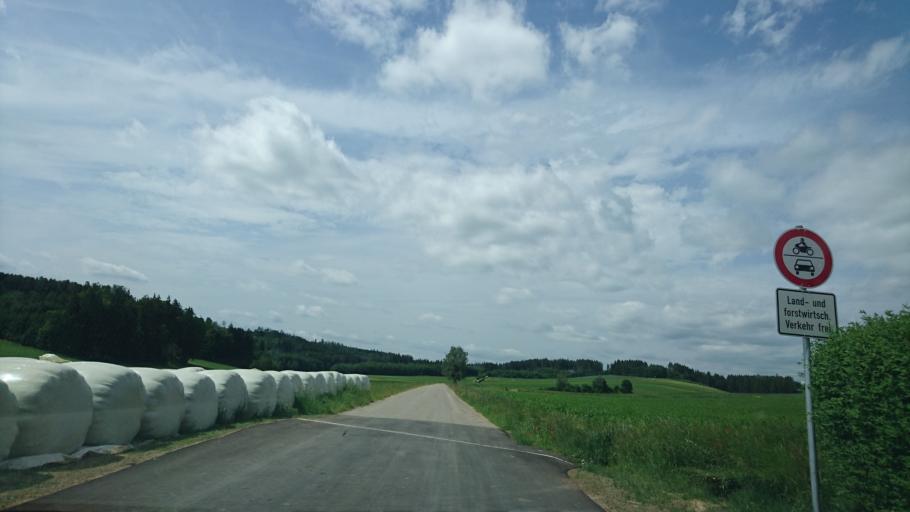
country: DE
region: Bavaria
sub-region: Swabia
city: Zusmarshausen
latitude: 48.4017
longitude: 10.5712
